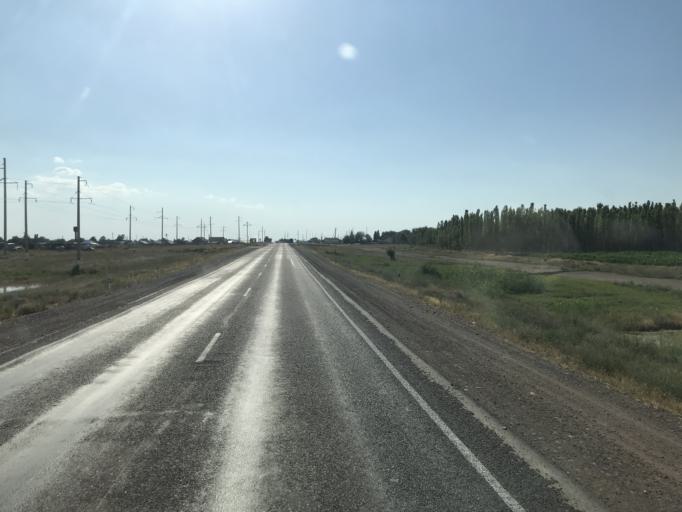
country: KG
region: Chuy
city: Sokuluk
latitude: 43.2458
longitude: 74.3055
